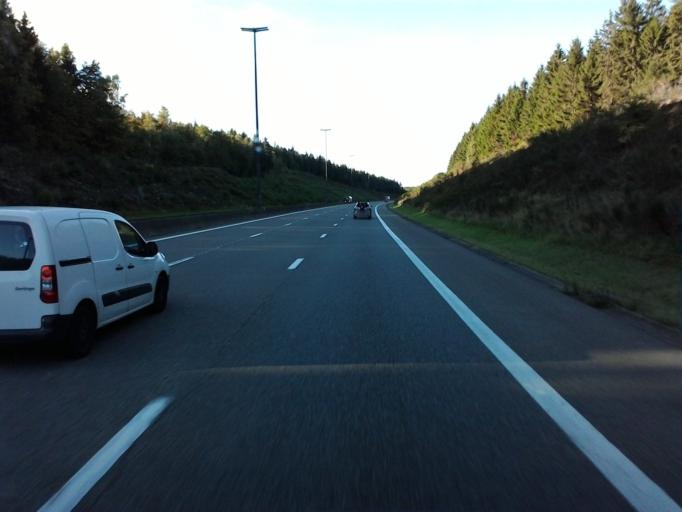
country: BE
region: Wallonia
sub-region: Province du Luxembourg
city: Houffalize
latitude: 50.1844
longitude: 5.7822
